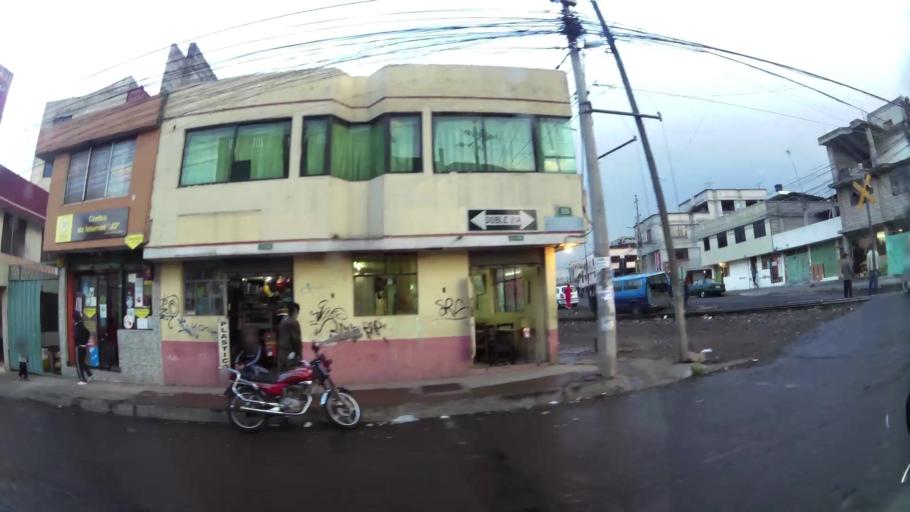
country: EC
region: Pichincha
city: Quito
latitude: -0.3045
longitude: -78.5399
